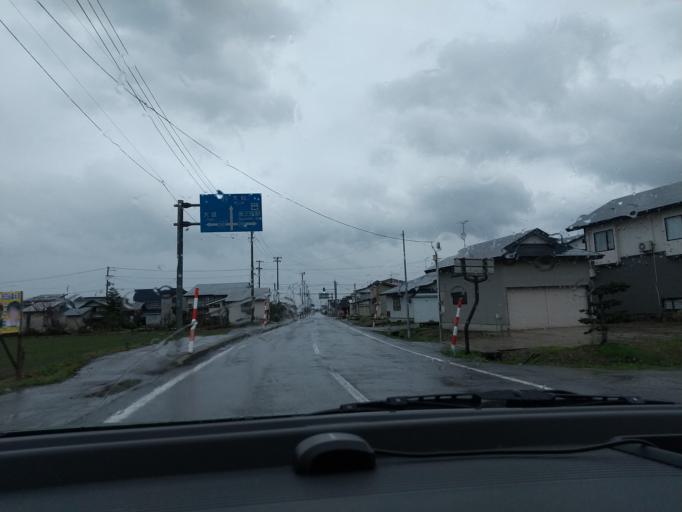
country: JP
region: Akita
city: Yokotemachi
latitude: 39.3638
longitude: 140.5360
